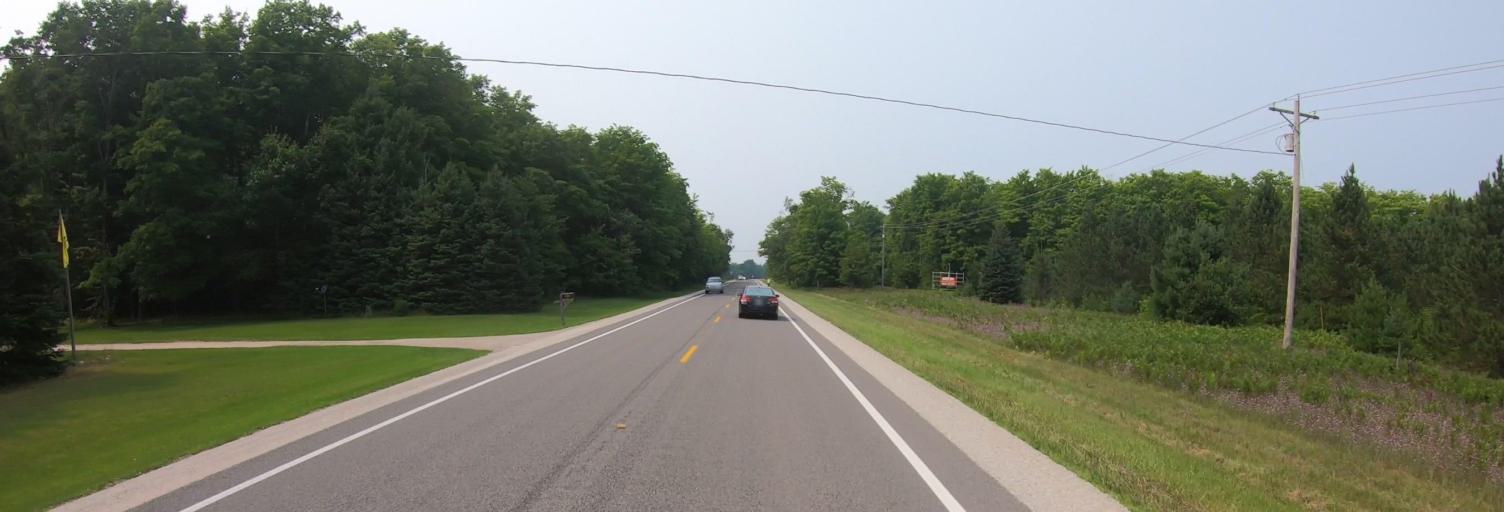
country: US
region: Michigan
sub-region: Chippewa County
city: Sault Ste. Marie
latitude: 46.0244
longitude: -84.0755
